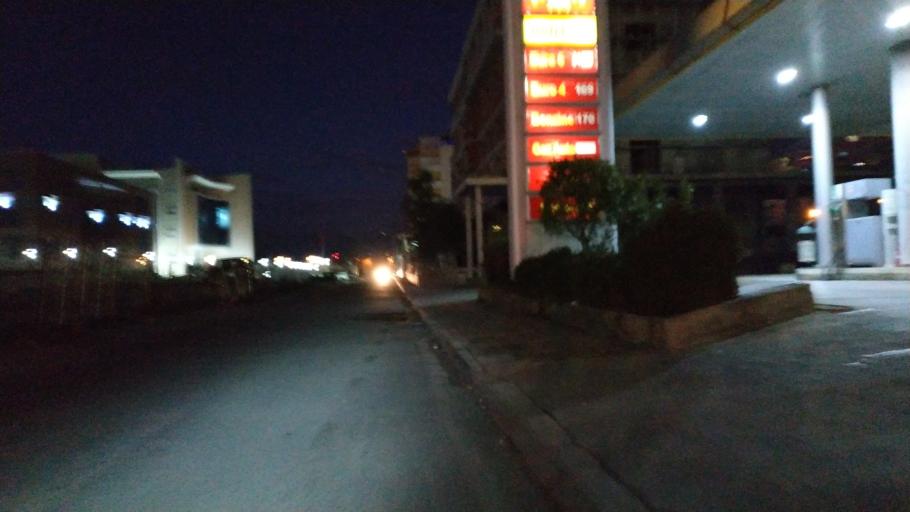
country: AL
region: Shkoder
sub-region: Rrethi i Shkodres
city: Shkoder
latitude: 42.0551
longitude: 19.4990
